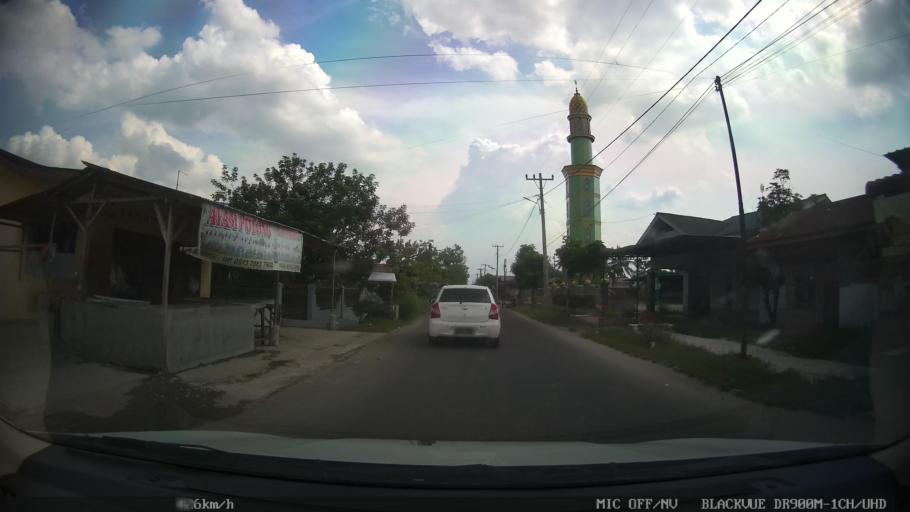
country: ID
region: North Sumatra
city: Binjai
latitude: 3.6277
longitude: 98.5014
